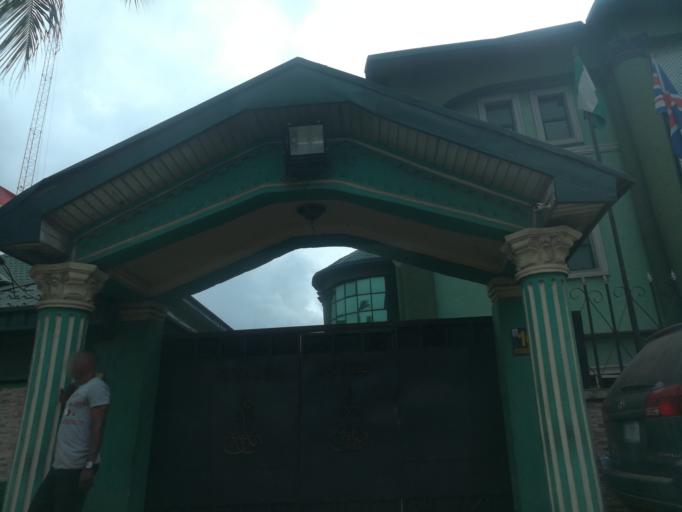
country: NG
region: Lagos
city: Ikeja
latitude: 6.5973
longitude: 3.3354
